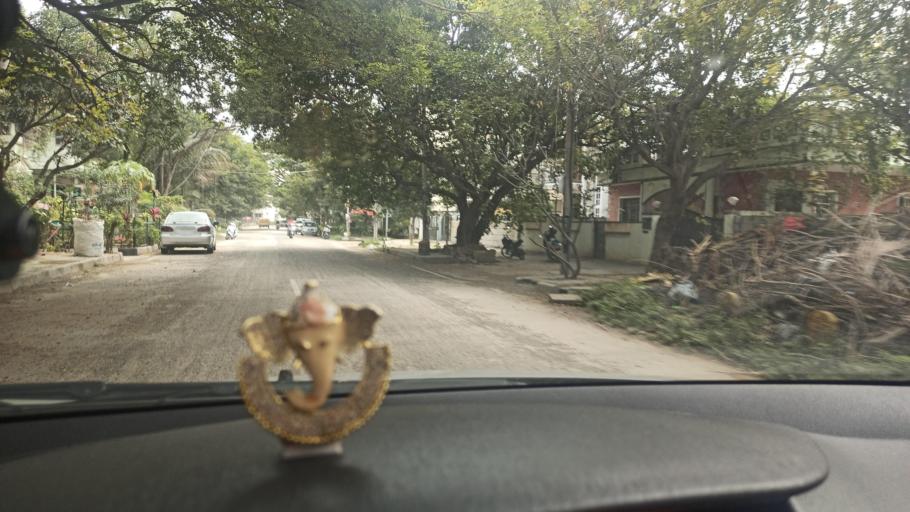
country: IN
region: Karnataka
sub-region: Bangalore Urban
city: Bangalore
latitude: 12.9156
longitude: 77.6261
